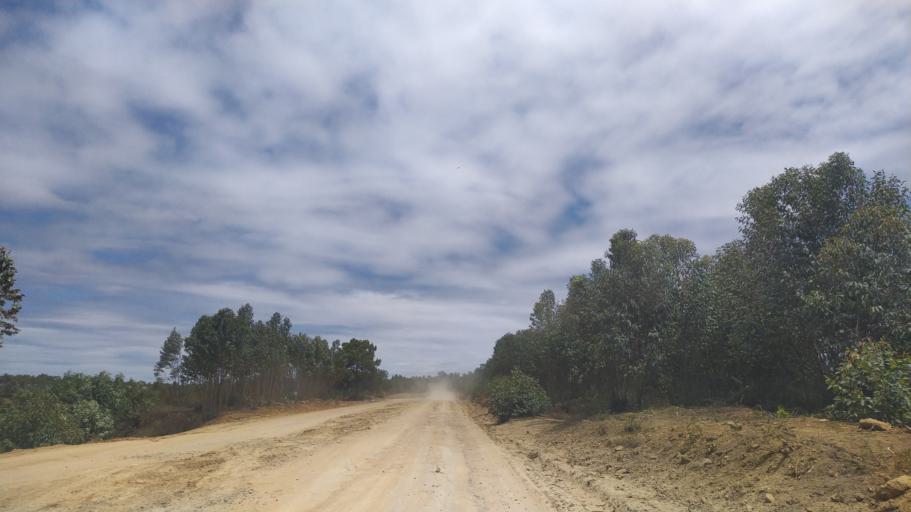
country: MG
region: Alaotra Mangoro
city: Moramanga
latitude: -18.6561
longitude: 48.2744
